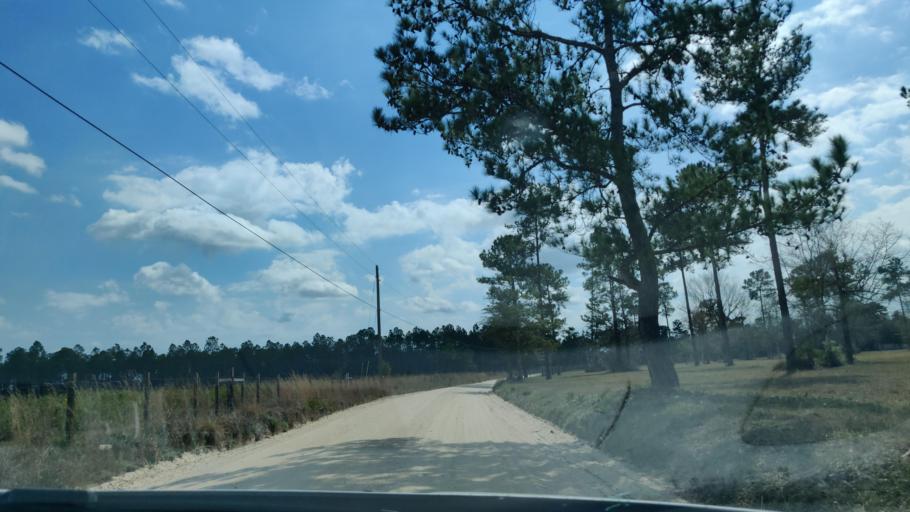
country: US
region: Florida
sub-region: Duval County
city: Baldwin
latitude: 30.1787
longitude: -81.9598
